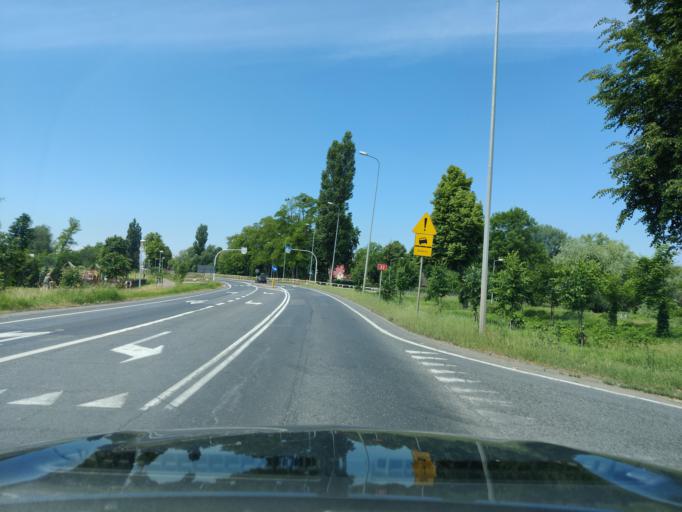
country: PL
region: Greater Poland Voivodeship
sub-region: Powiat grodziski
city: Kamieniec
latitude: 52.2268
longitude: 16.4439
